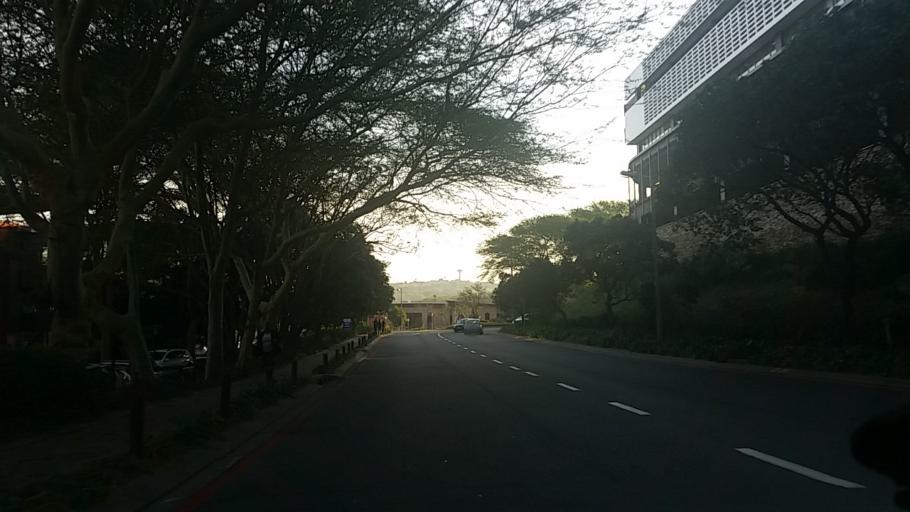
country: ZA
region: KwaZulu-Natal
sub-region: eThekwini Metropolitan Municipality
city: Berea
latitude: -29.8497
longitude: 30.9300
